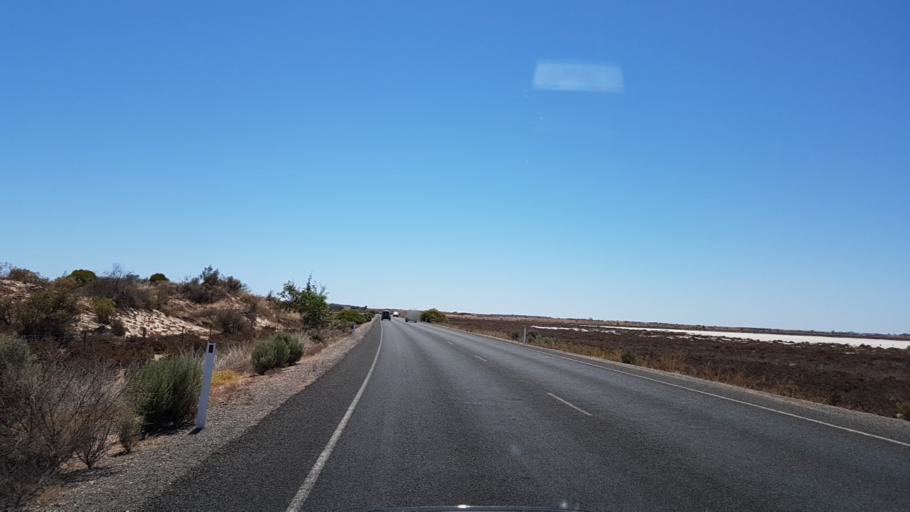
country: AU
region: South Australia
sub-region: Copper Coast
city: Wallaroo
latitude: -33.9192
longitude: 137.6453
